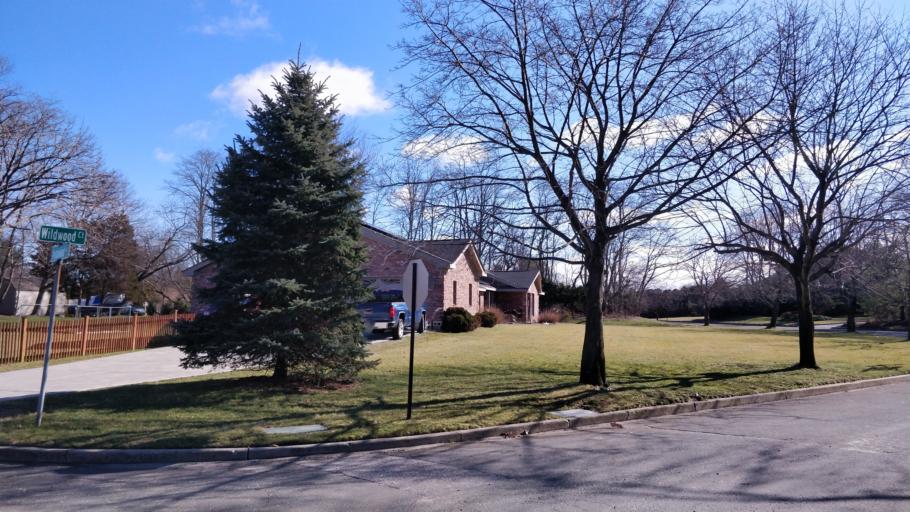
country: US
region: New York
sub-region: Suffolk County
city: Saint James
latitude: 40.8836
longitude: -73.1439
